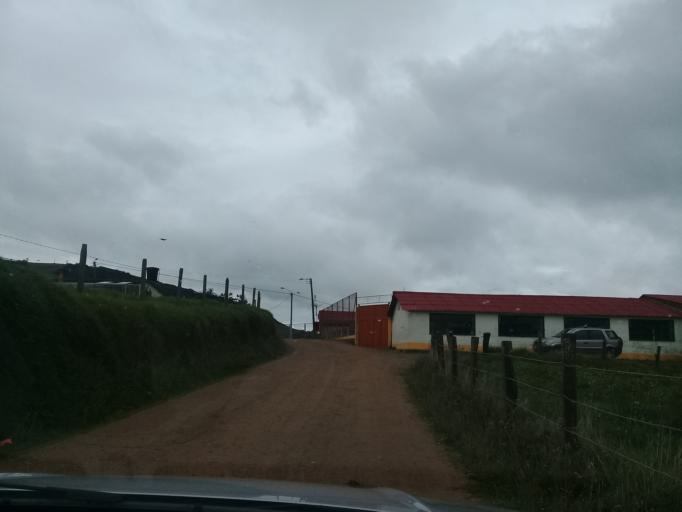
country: CO
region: Boyaca
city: Samaca
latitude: 5.4543
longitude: -73.4414
